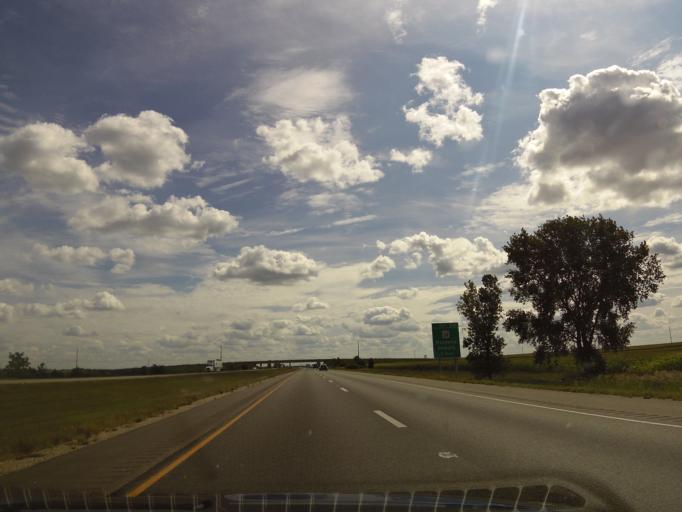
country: US
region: Illinois
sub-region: Ogle County
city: Hillcrest
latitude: 41.9533
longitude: -89.0246
